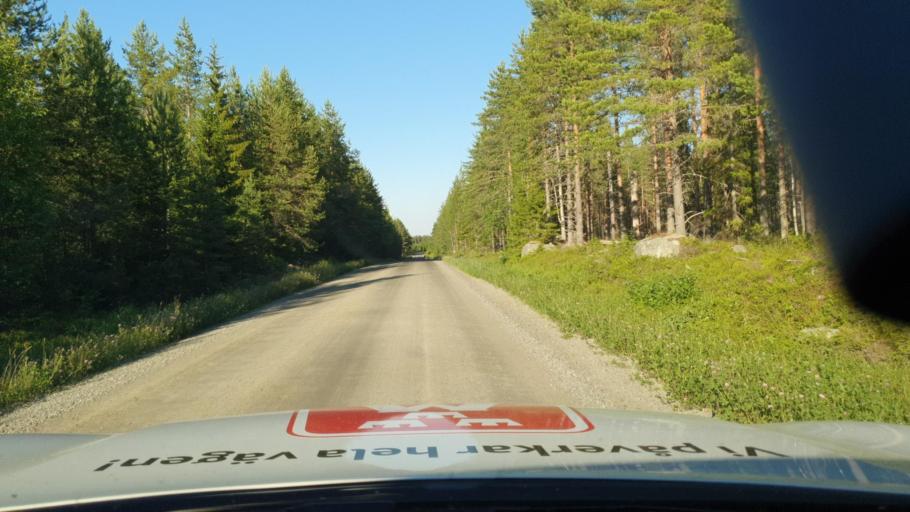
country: SE
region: Vaesterbotten
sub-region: Skelleftea Kommun
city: Burea
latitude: 64.5080
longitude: 21.3211
